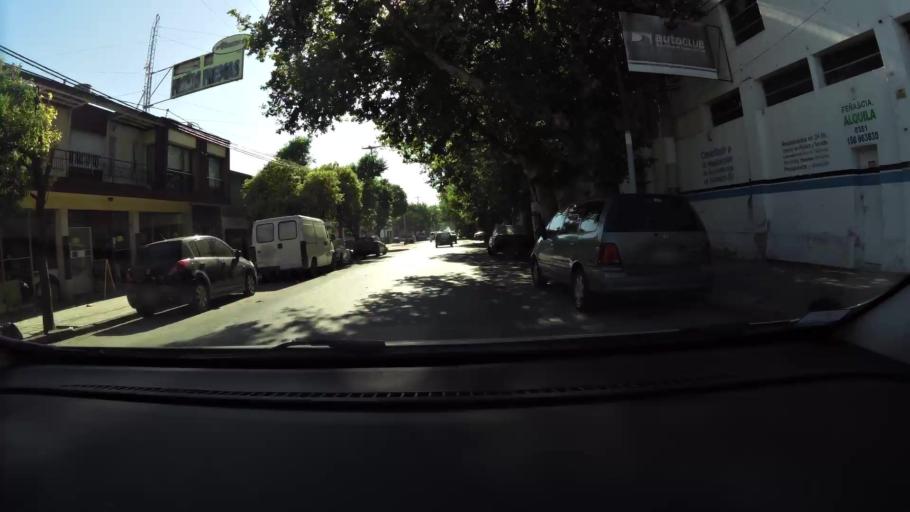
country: AR
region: Cordoba
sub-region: Departamento de Capital
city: Cordoba
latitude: -31.4243
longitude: -64.1615
